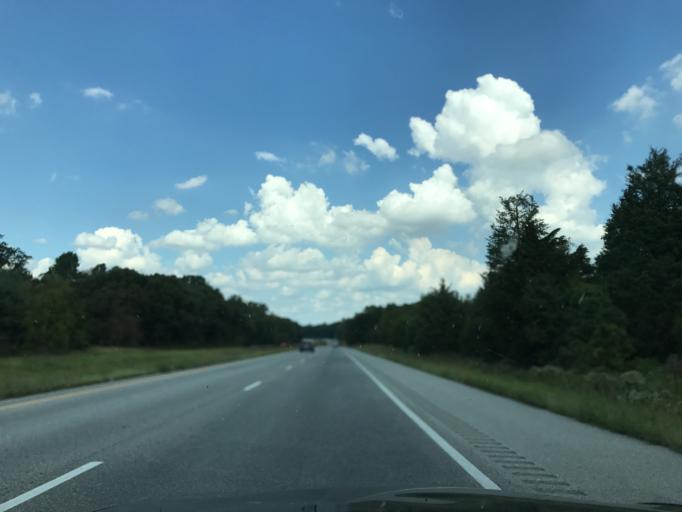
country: US
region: Maryland
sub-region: Queen Anne's County
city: Kingstown
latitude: 39.2506
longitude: -75.8687
